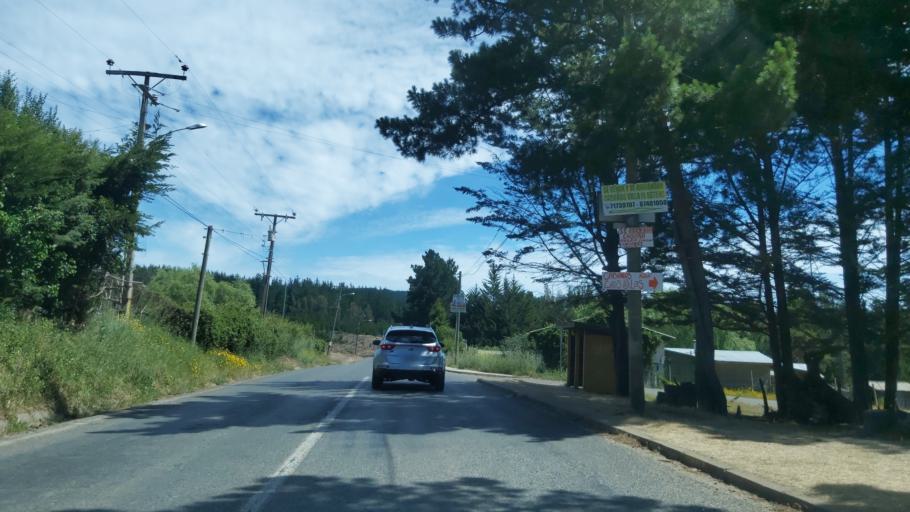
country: CL
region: Maule
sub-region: Provincia de Talca
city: Constitucion
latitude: -35.5058
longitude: -72.5204
